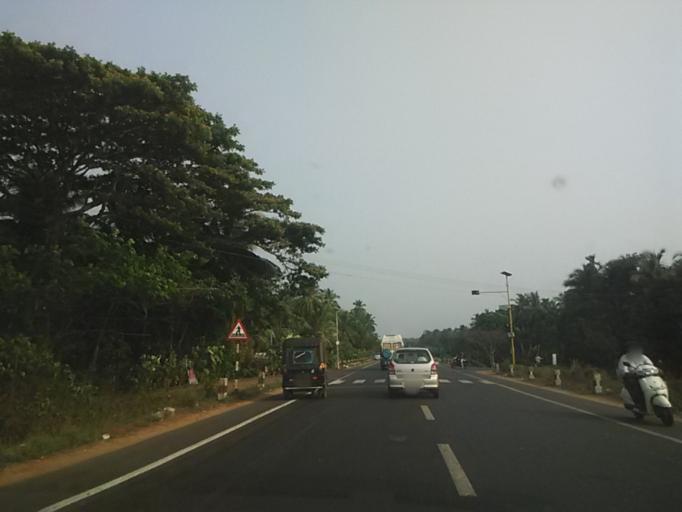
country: IN
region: Kerala
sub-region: Kozhikode
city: Kozhikode
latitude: 11.3157
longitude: 75.7795
